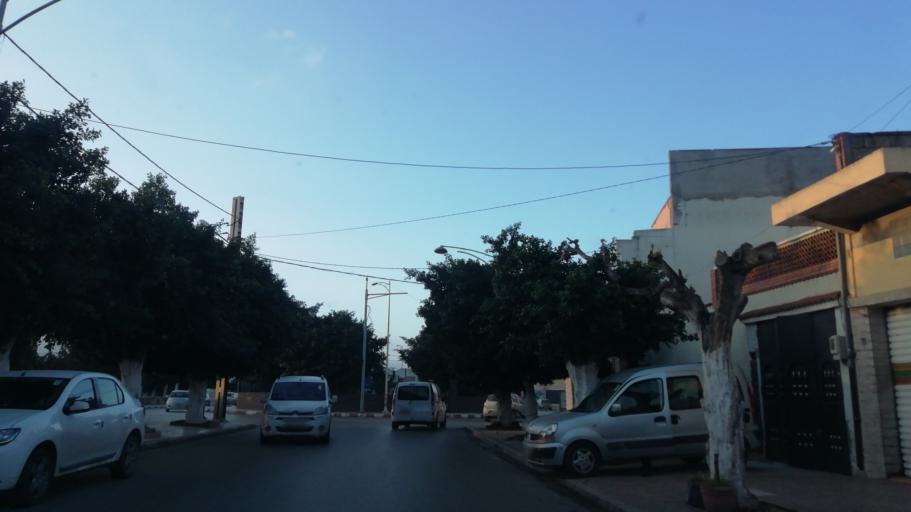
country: DZ
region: Oran
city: Oran
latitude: 35.6791
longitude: -0.6565
